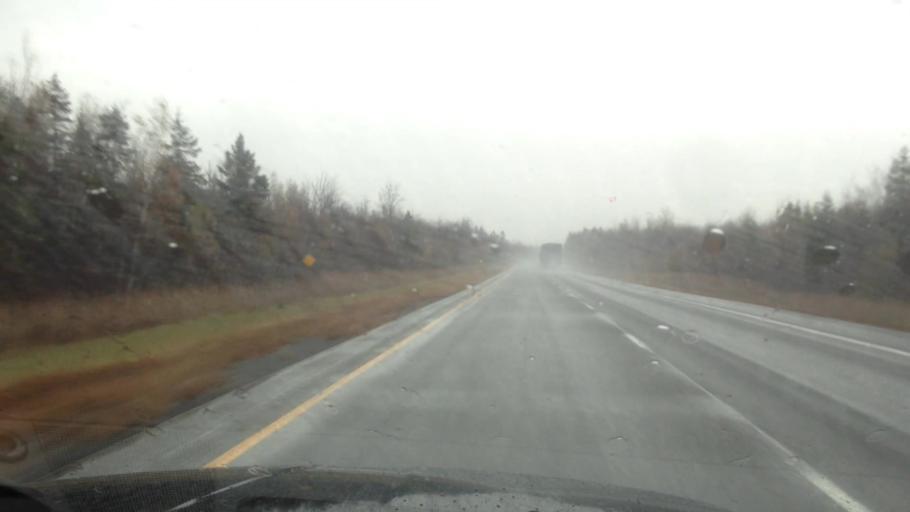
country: CA
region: Ontario
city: Casselman
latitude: 45.3132
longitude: -75.2030
